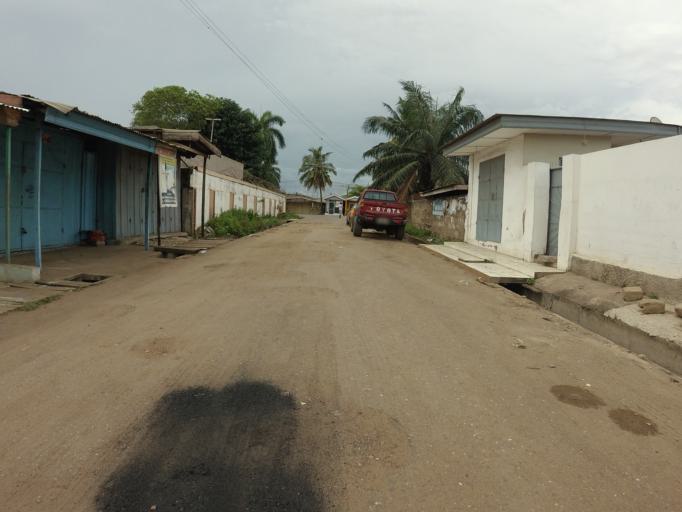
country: GH
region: Greater Accra
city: Accra
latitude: 5.5980
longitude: -0.2146
